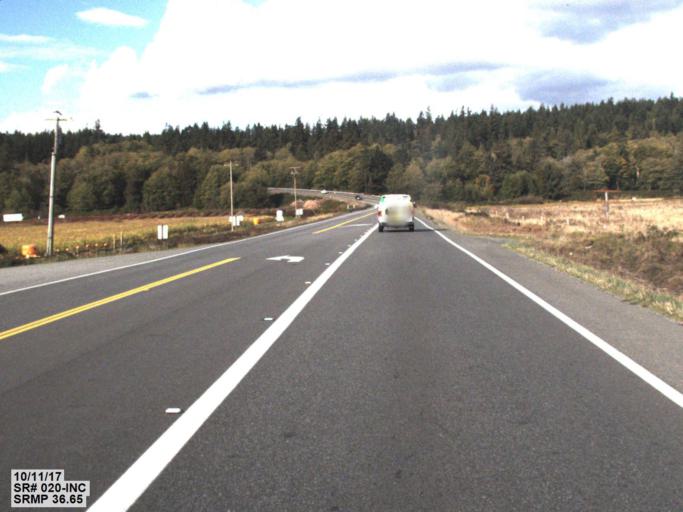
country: US
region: Washington
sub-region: Island County
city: Ault Field
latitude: 48.3512
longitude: -122.6123
